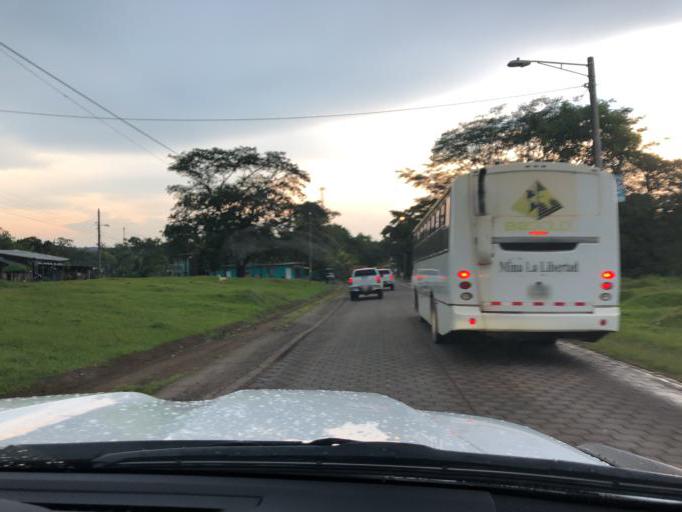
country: NI
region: Chontales
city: La Libertad
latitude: 12.2130
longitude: -85.1720
